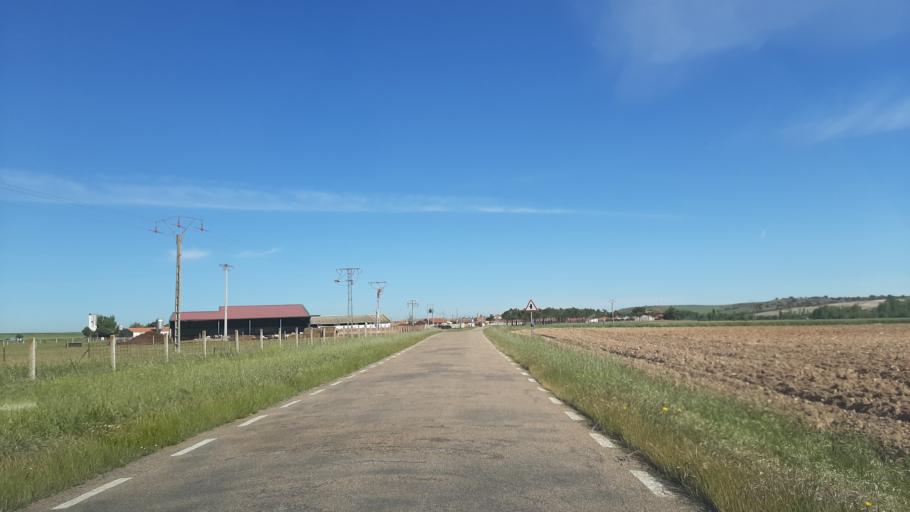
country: ES
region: Castille and Leon
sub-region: Provincia de Salamanca
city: Pedrosillo de Alba
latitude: 40.8044
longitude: -5.3798
